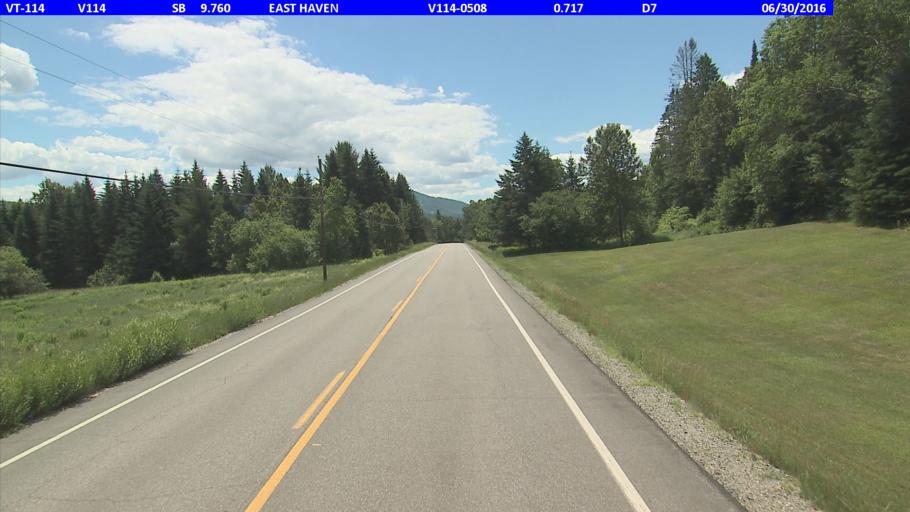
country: US
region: Vermont
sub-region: Caledonia County
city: Lyndonville
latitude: 44.6489
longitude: -71.8926
